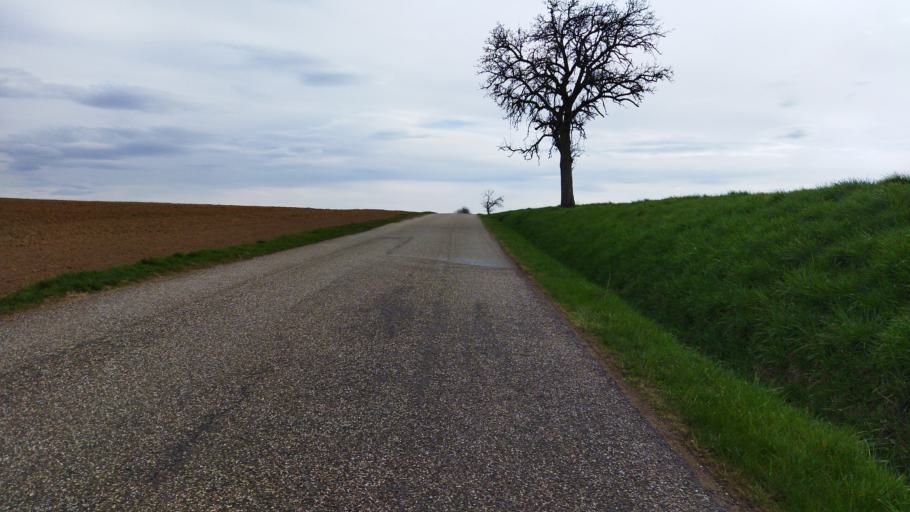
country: DE
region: Baden-Wuerttemberg
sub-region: Regierungsbezirk Stuttgart
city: Neudenau
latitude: 49.3007
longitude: 9.2289
